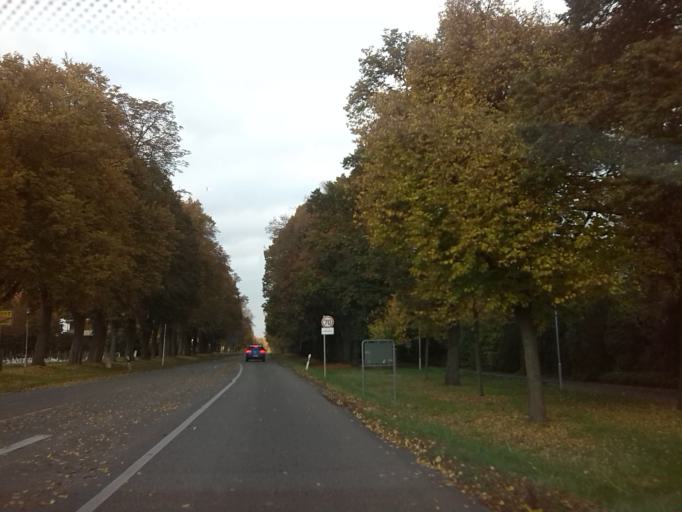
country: DE
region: Baden-Wuerttemberg
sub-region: Regierungsbezirk Stuttgart
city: Kornwestheim
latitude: 48.8690
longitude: 9.1861
